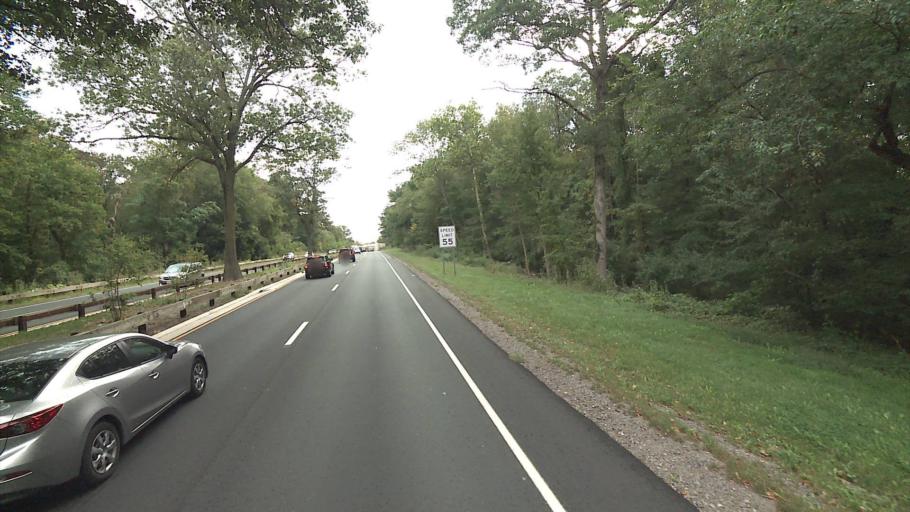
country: US
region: Connecticut
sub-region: Fairfield County
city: North Stamford
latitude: 41.1149
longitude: -73.5385
